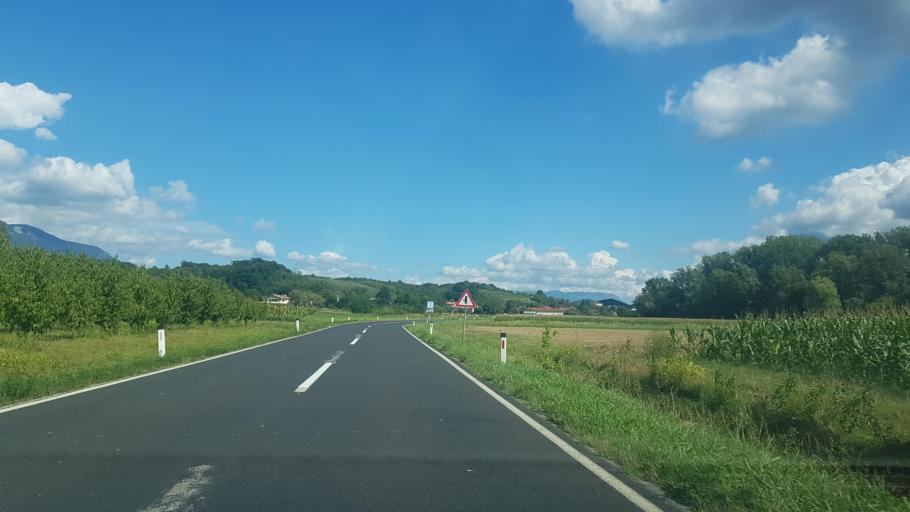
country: SI
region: Nova Gorica
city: Prvacina
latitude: 45.8957
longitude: 13.6989
